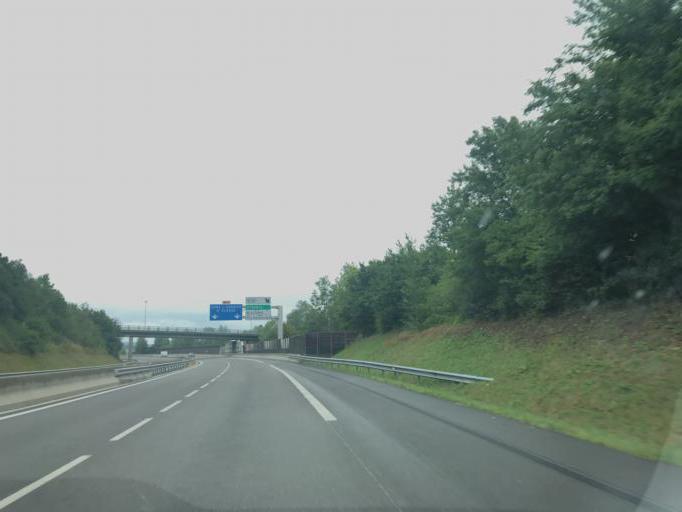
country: FR
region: Rhone-Alpes
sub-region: Departement de l'Ain
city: Groissiat
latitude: 46.2271
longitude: 5.6177
